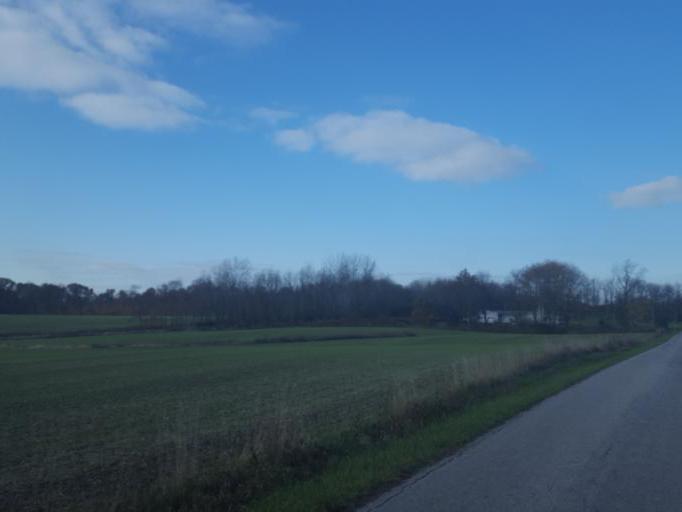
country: US
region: Ohio
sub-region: Crawford County
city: Galion
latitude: 40.6386
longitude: -82.7199
